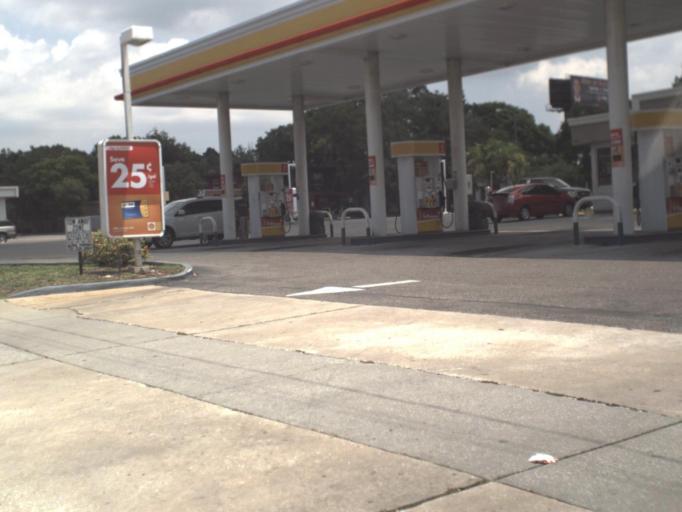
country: US
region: Florida
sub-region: Pinellas County
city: Saint Petersburg
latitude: 27.7513
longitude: -82.6793
